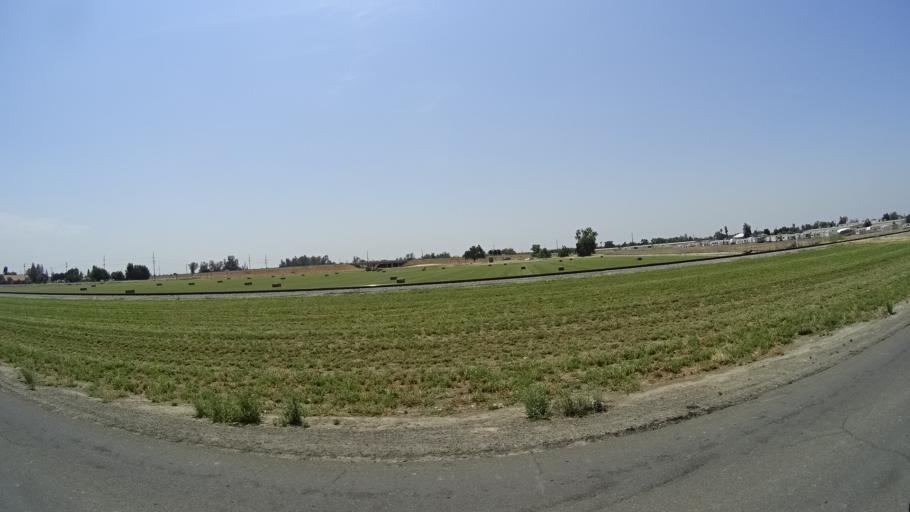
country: US
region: California
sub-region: Kings County
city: Armona
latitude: 36.3180
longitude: -119.6944
